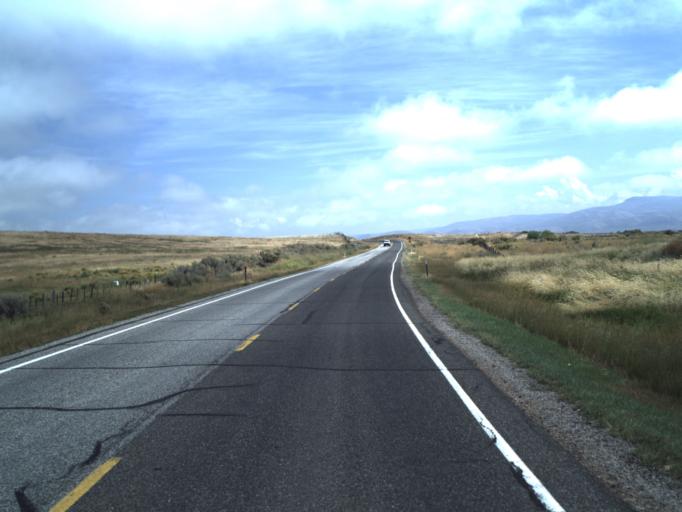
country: US
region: Utah
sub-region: Rich County
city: Randolph
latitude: 41.6984
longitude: -111.1686
